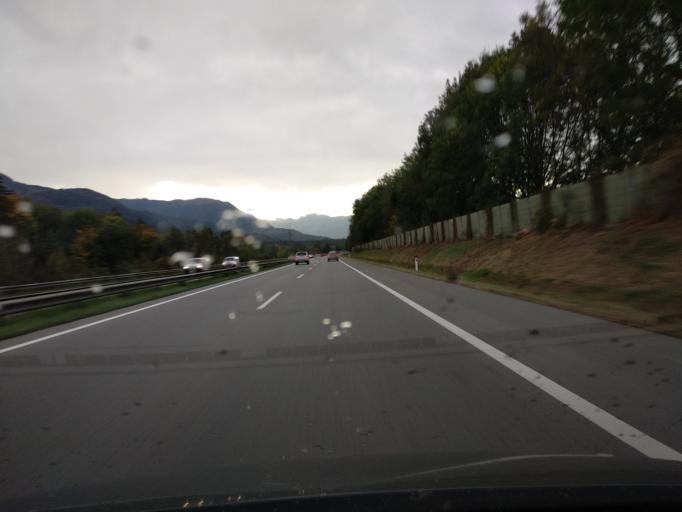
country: AT
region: Vorarlberg
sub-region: Politischer Bezirk Feldkirch
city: Schlins
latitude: 47.1987
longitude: 9.6875
